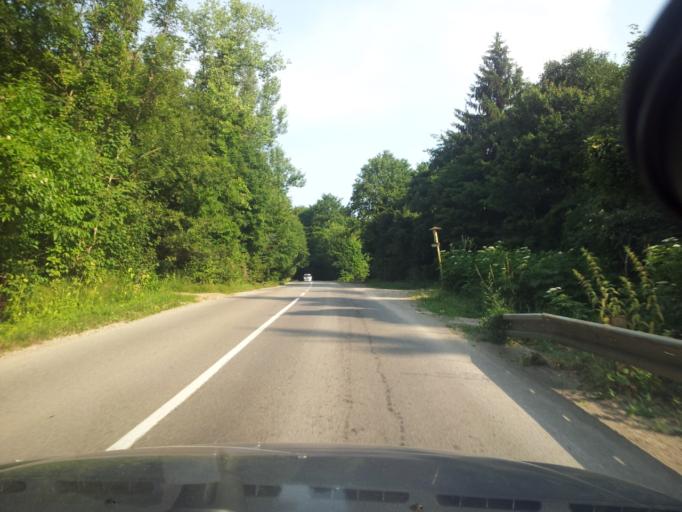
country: SK
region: Nitriansky
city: Trencianske Teplice
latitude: 48.8921
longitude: 18.1764
